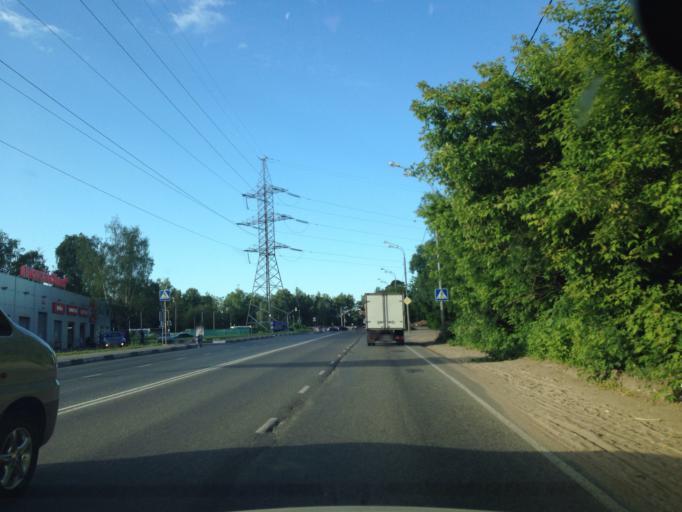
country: RU
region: Moscow
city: Vostochnyy
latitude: 55.7921
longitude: 37.8950
